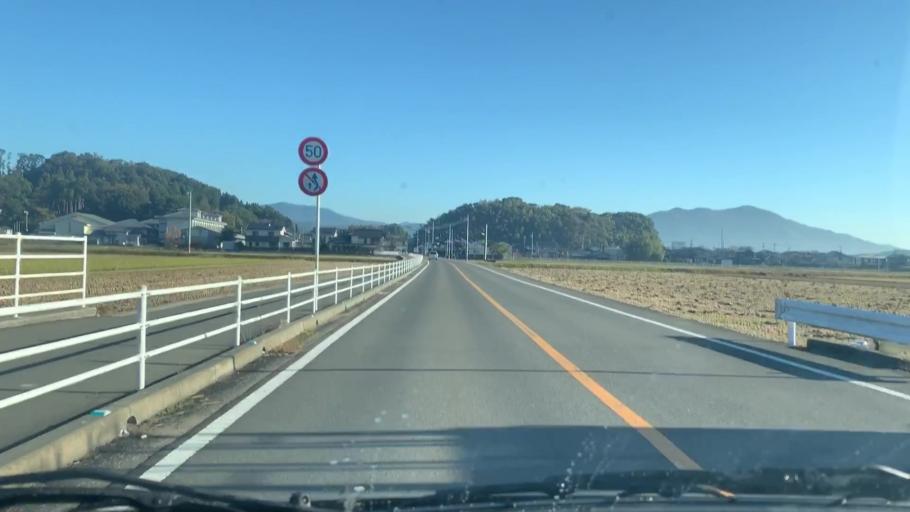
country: JP
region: Saga Prefecture
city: Takeocho-takeo
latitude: 33.2110
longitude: 130.0368
